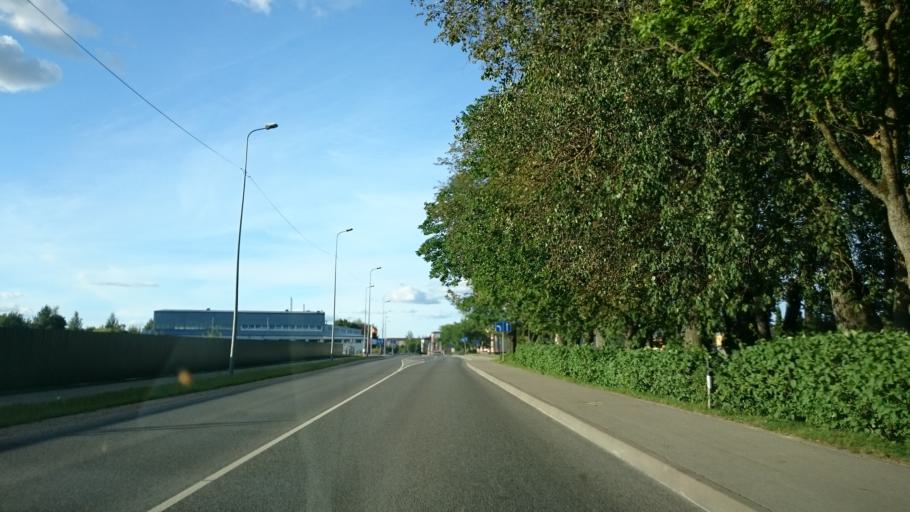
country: LV
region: Saldus Rajons
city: Saldus
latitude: 56.6576
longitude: 22.4733
